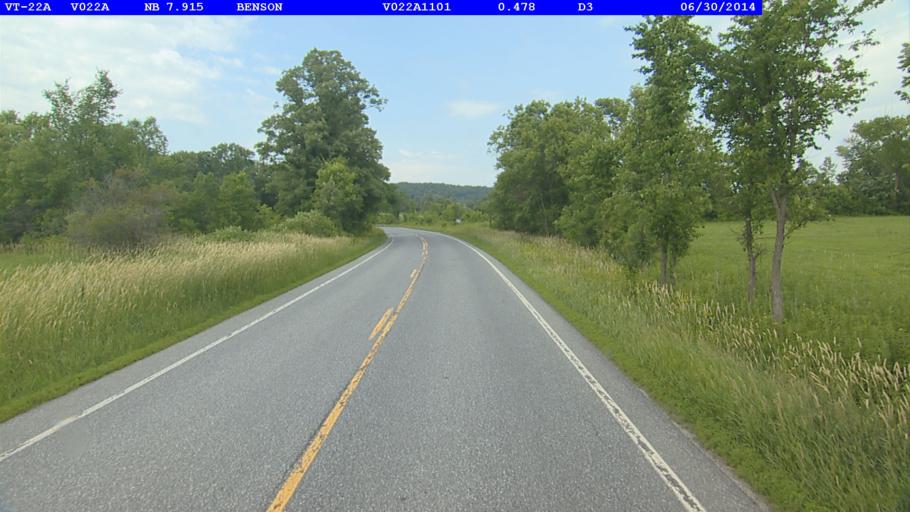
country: US
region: Vermont
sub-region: Rutland County
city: Fair Haven
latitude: 43.6762
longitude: -73.2885
